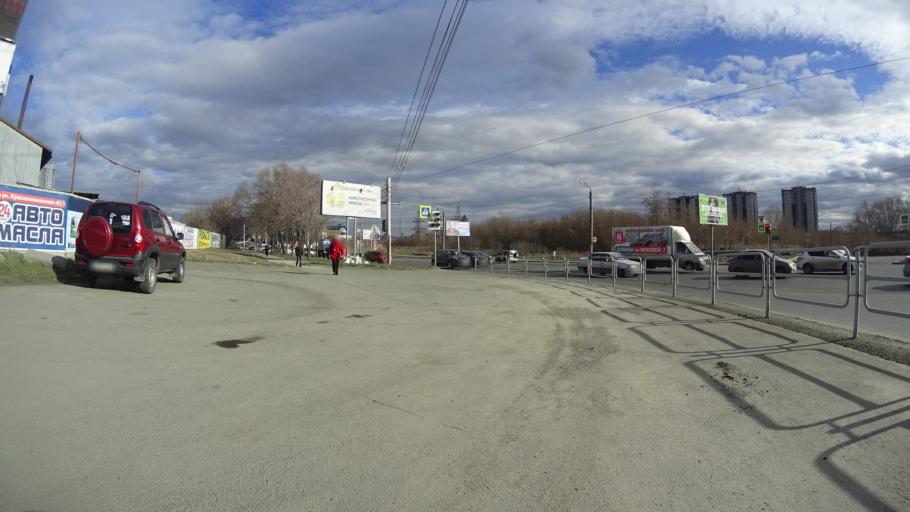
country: RU
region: Chelyabinsk
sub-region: Gorod Chelyabinsk
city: Chelyabinsk
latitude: 55.1754
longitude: 61.3805
